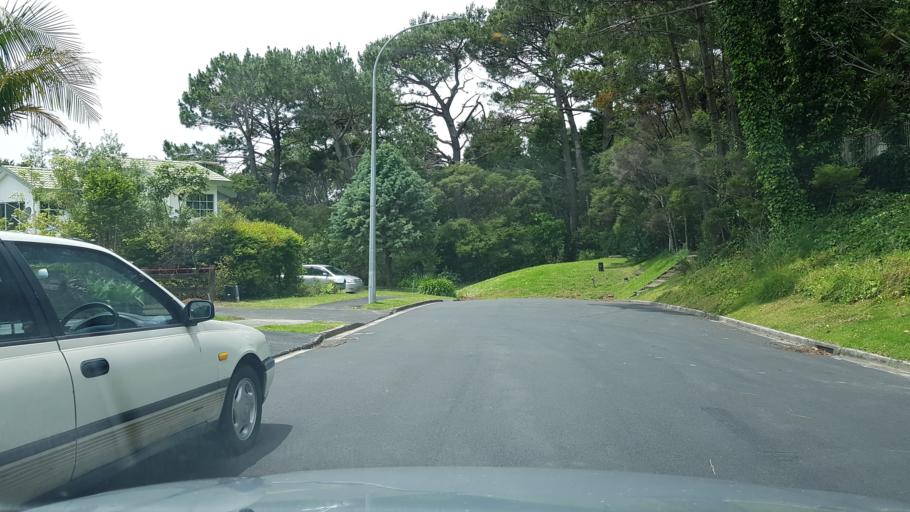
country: NZ
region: Auckland
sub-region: Auckland
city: North Shore
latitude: -36.8218
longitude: 174.7155
